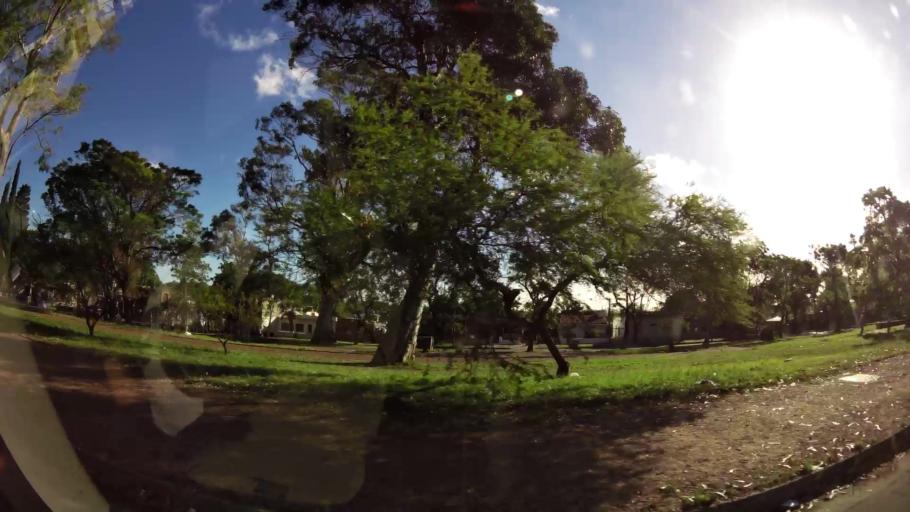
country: UY
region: Montevideo
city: Montevideo
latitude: -34.8564
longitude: -56.2316
